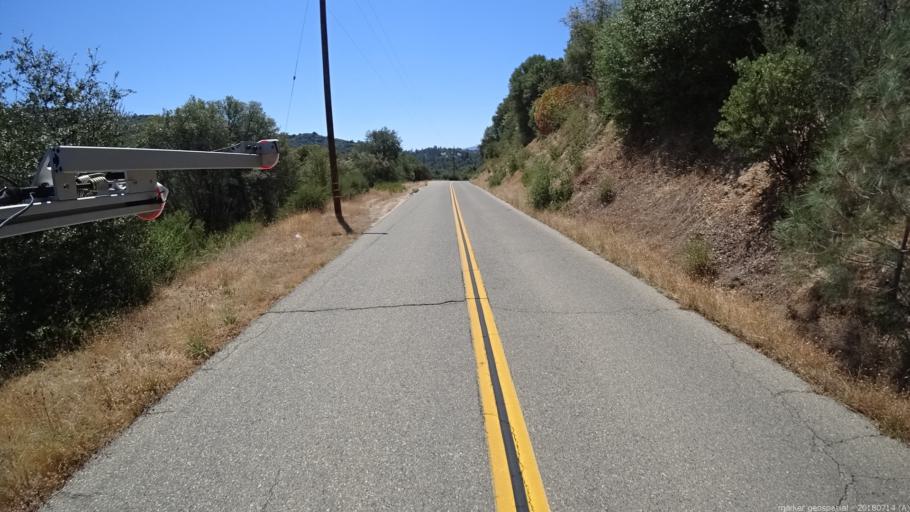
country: US
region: California
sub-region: Madera County
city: Oakhurst
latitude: 37.3796
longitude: -119.6713
